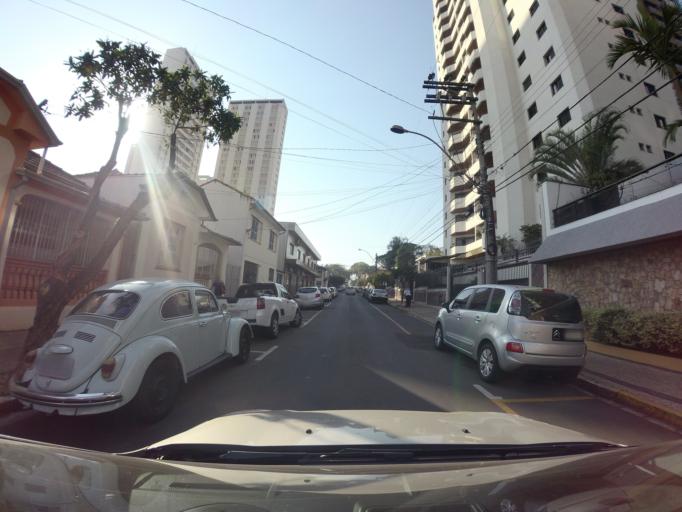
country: BR
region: Sao Paulo
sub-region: Piracicaba
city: Piracicaba
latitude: -22.7312
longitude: -47.6547
